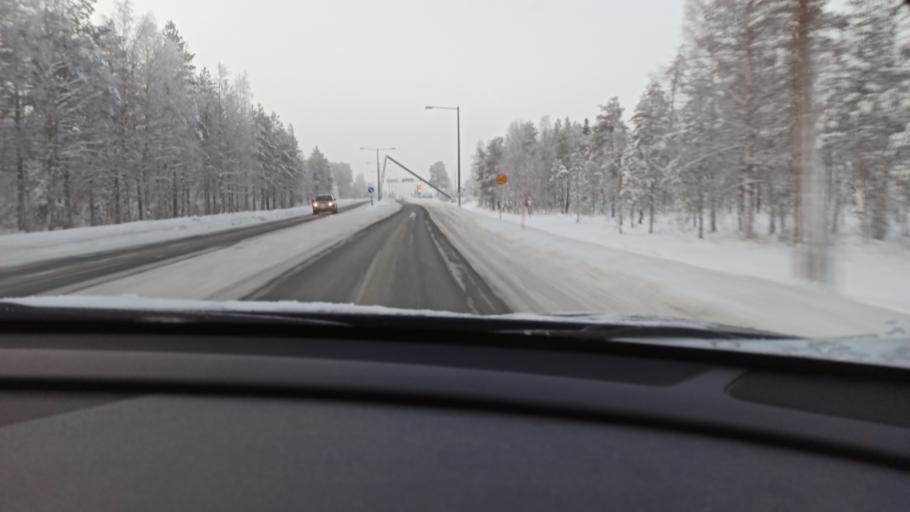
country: FI
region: Lapland
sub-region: Rovaniemi
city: Rovaniemi
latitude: 66.5461
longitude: 25.8573
